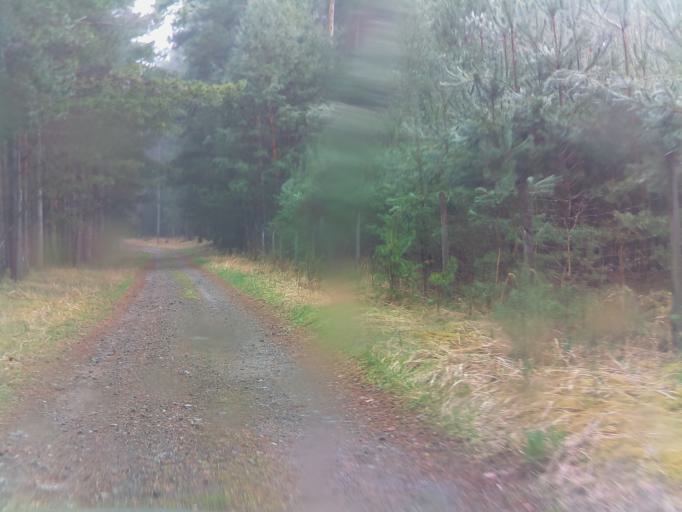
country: DE
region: Brandenburg
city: Lieberose
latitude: 52.0221
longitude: 14.2381
